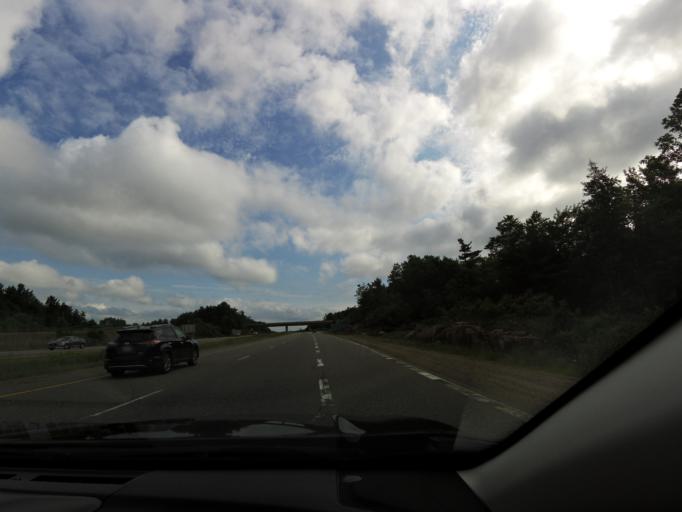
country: CA
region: Ontario
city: Bracebridge
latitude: 45.0092
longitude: -79.2981
